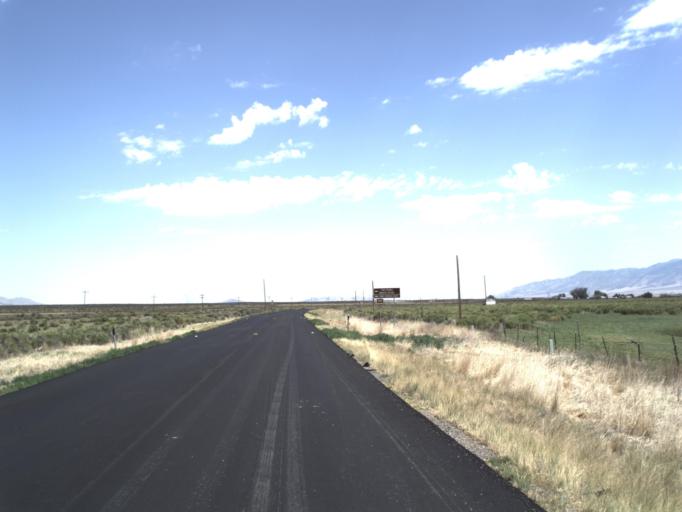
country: US
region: Utah
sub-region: Tooele County
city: Tooele
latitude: 40.1601
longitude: -112.4307
